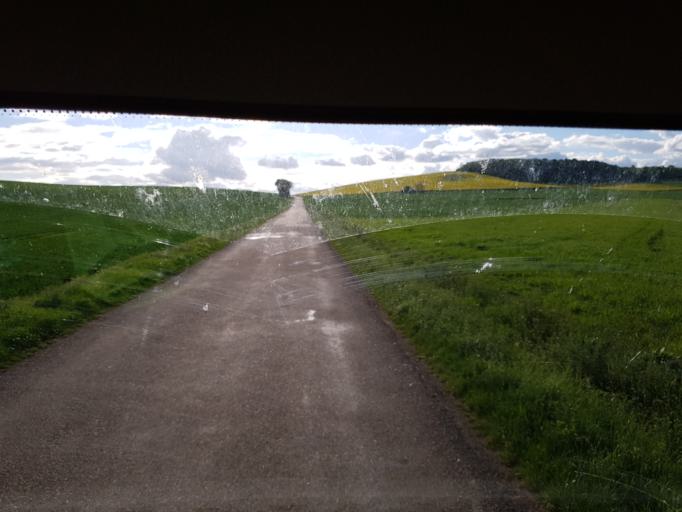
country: FR
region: Bourgogne
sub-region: Departement de l'Yonne
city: Saint-Florentin
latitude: 48.0641
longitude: 3.7338
